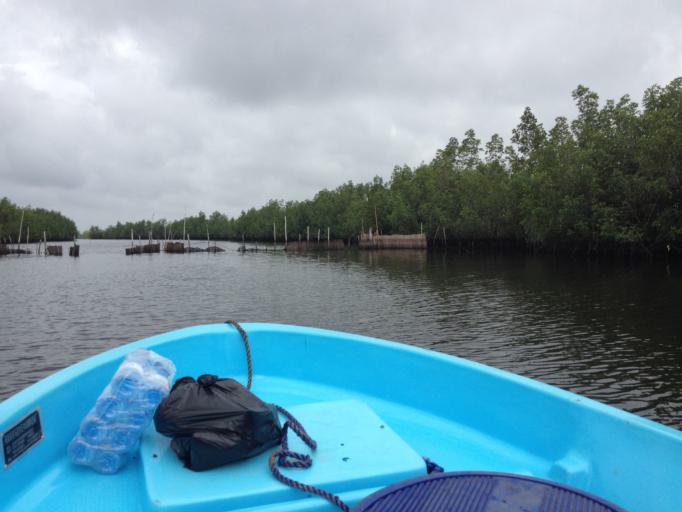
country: BJ
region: Mono
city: Come
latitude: 6.3807
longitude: 1.9374
